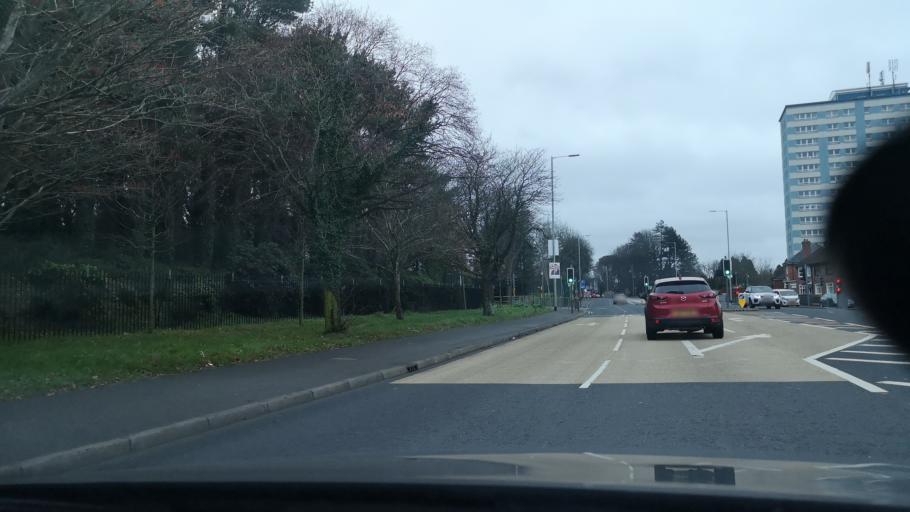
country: GB
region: Northern Ireland
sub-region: Castlereagh District
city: Dundonald
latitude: 54.5941
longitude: -5.8258
